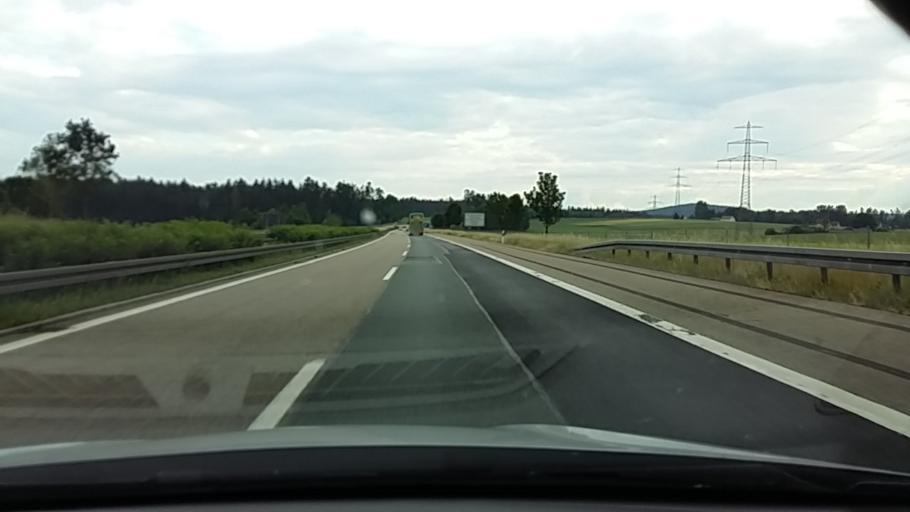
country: DE
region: Bavaria
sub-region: Upper Palatinate
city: Waidhaus
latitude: 49.6389
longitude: 12.5161
